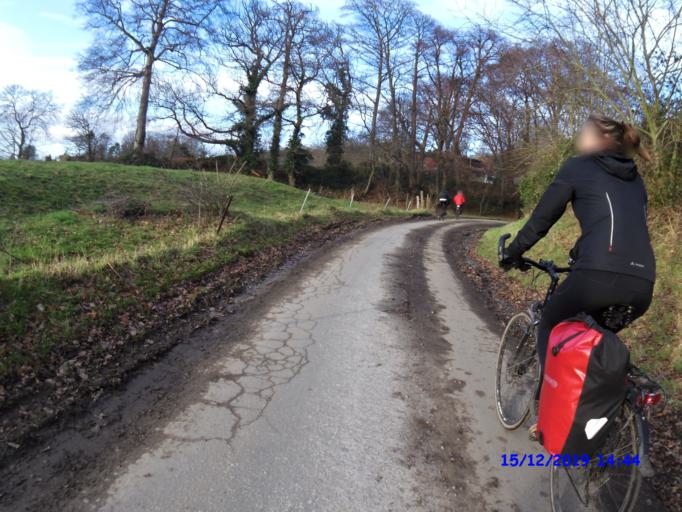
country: BE
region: Flanders
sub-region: Provincie Vlaams-Brabant
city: Beersel
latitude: 50.7525
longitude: 4.3132
